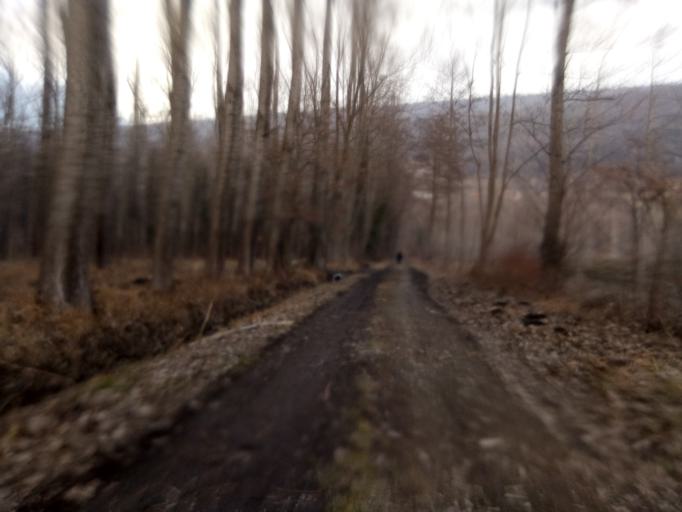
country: IT
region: Piedmont
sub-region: Provincia di Torino
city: Cascinette d'Ivrea
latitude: 45.4884
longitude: 7.9182
